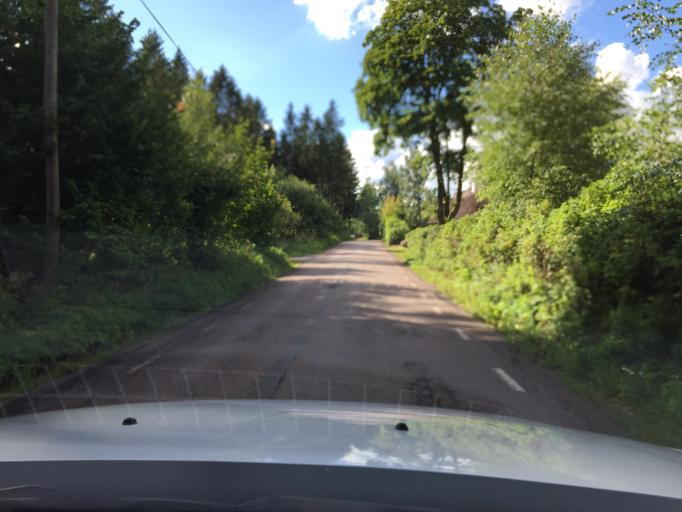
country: SE
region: Skane
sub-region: Hassleholms Kommun
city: Tormestorp
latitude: 56.0041
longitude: 13.7956
